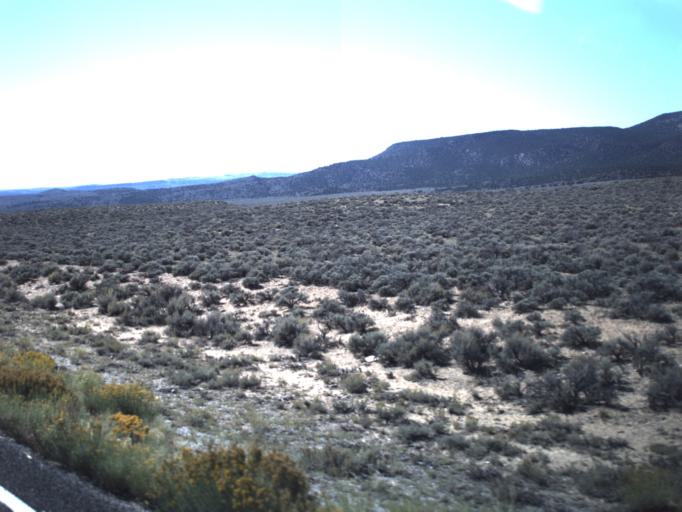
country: US
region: Utah
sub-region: Piute County
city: Junction
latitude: 38.2226
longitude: -111.9989
